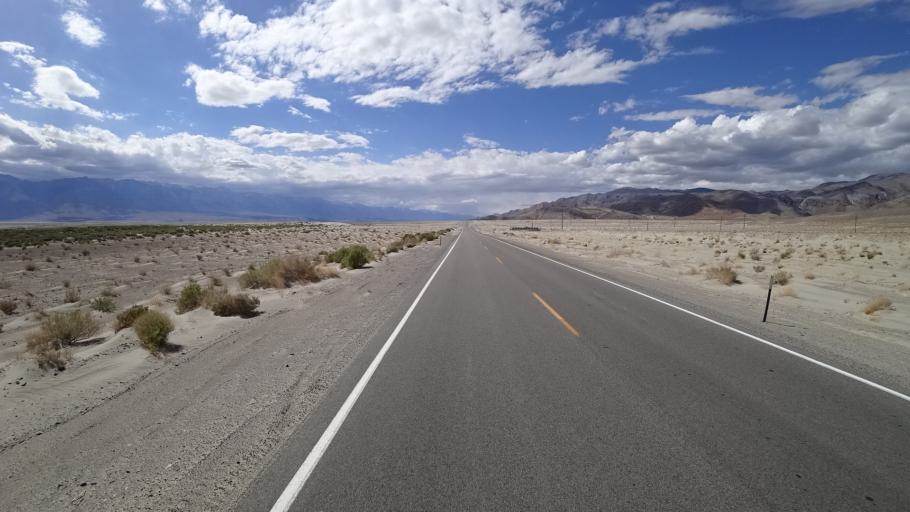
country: US
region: California
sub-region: Inyo County
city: Lone Pine
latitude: 36.4948
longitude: -117.8769
